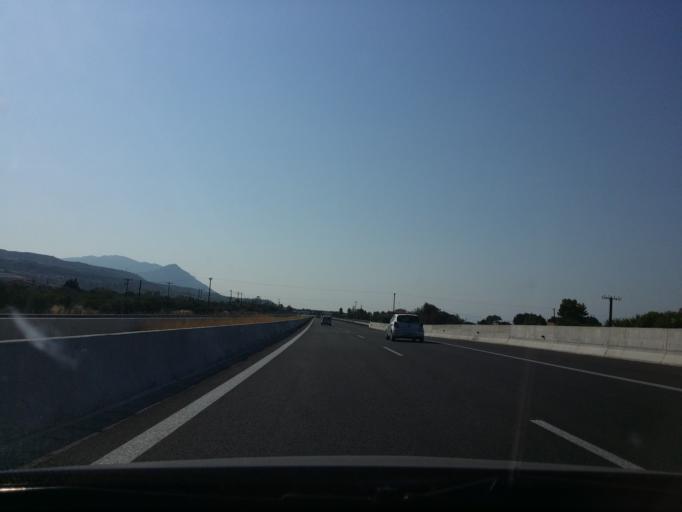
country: GR
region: Peloponnese
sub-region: Nomos Korinthias
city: Xylokastro
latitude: 38.0521
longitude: 22.6798
